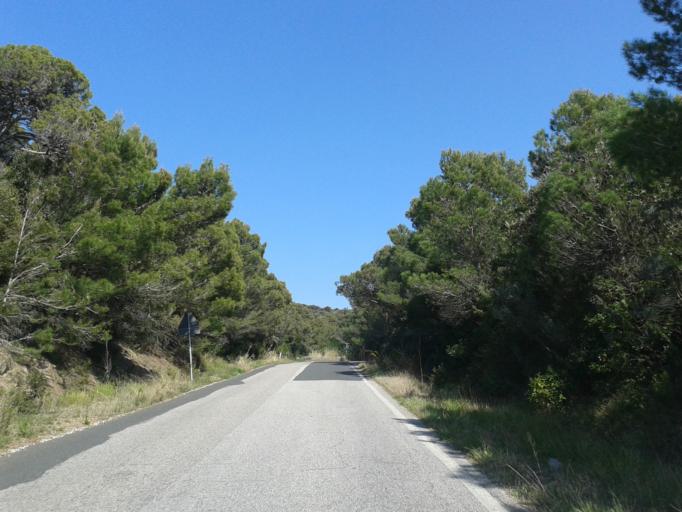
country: IT
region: Tuscany
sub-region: Provincia di Livorno
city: Quercianella
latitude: 43.4484
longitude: 10.3902
